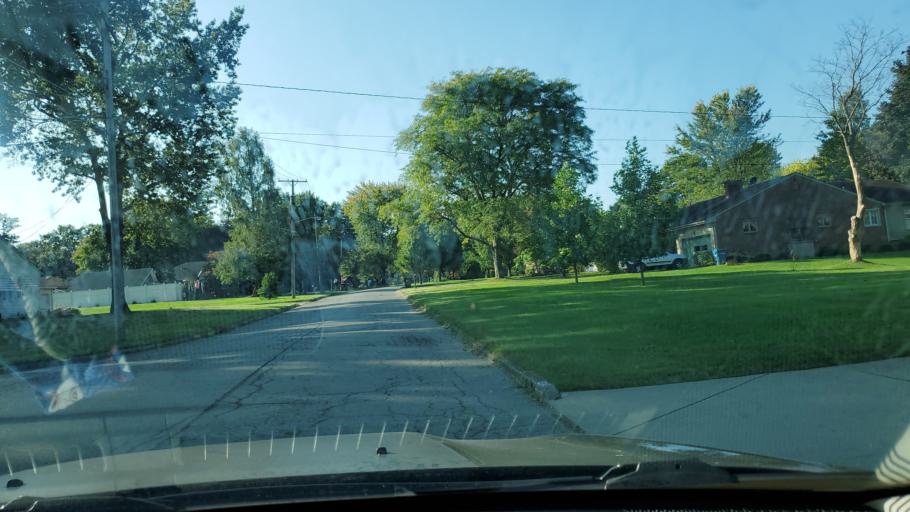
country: US
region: Ohio
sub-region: Mahoning County
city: Boardman
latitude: 41.0479
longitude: -80.6502
